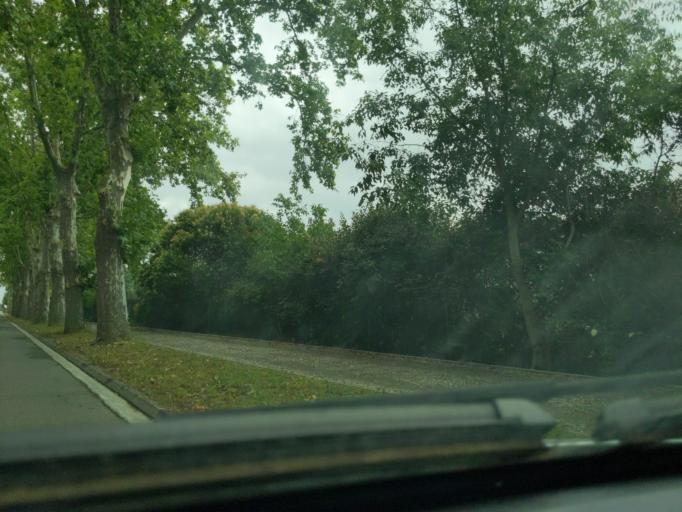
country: FR
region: Midi-Pyrenees
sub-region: Departement de la Haute-Garonne
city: Cugnaux
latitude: 43.5771
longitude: 1.3624
